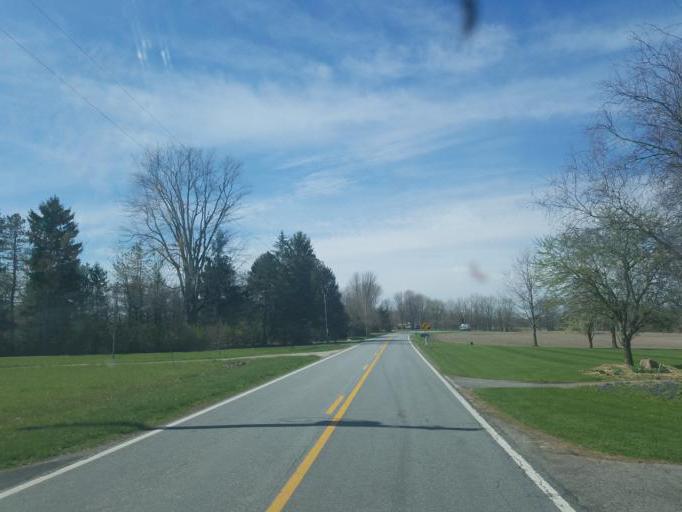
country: US
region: Ohio
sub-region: Delaware County
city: Ashley
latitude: 40.4028
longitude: -83.0290
